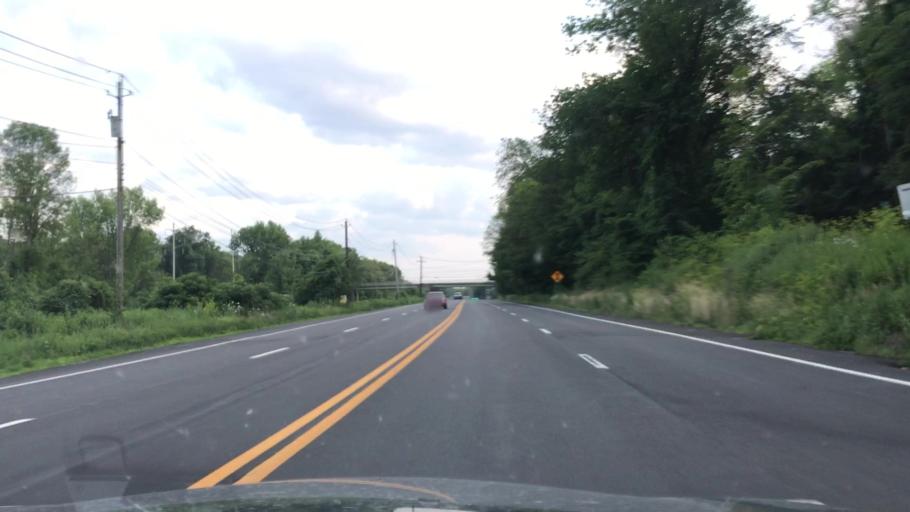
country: US
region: New York
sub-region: Rockland County
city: Sloatsburg
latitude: 41.2307
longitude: -74.1828
